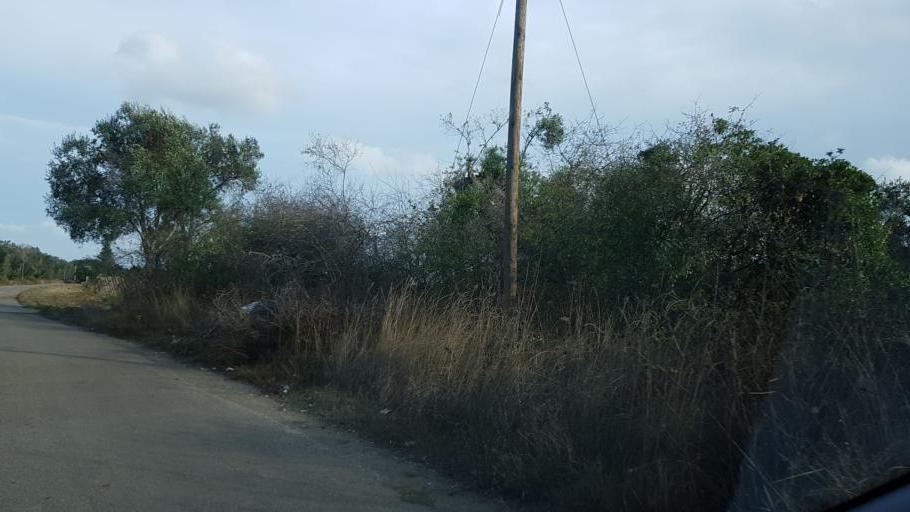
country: IT
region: Apulia
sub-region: Provincia di Brindisi
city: Oria
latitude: 40.5010
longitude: 17.6661
